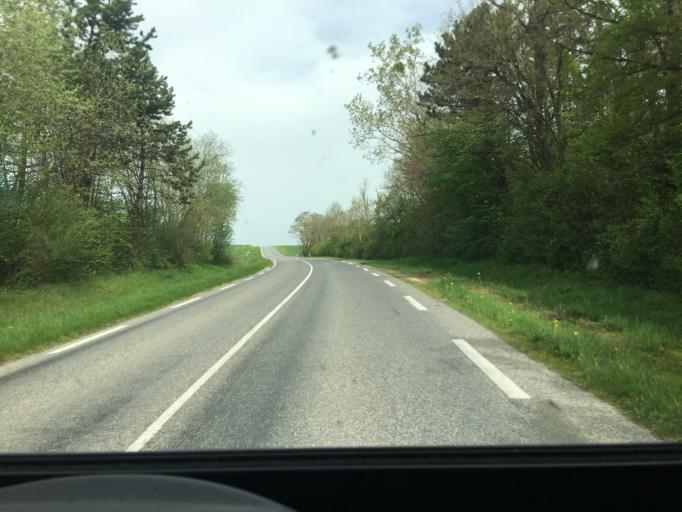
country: FR
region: Lorraine
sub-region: Departement de la Moselle
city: Vic-sur-Seille
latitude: 48.8024
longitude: 6.5537
